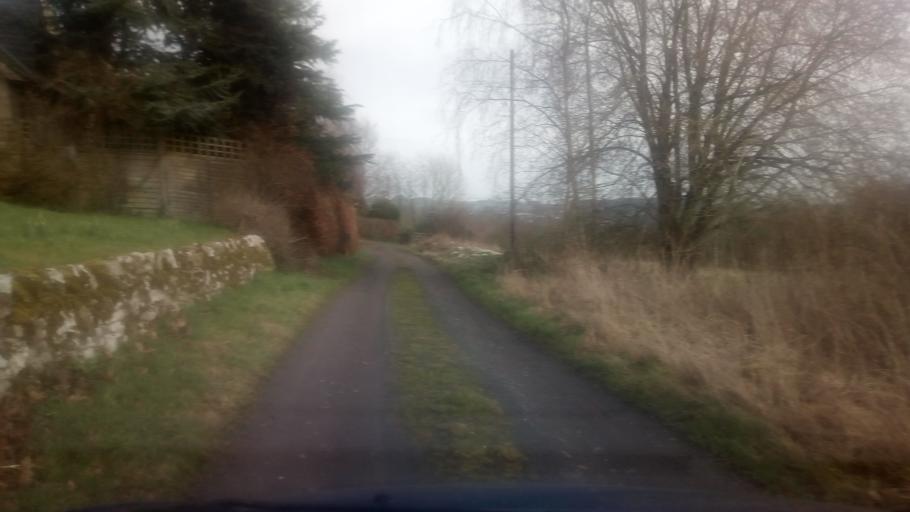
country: GB
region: Scotland
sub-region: The Scottish Borders
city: Jedburgh
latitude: 55.4600
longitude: -2.5682
